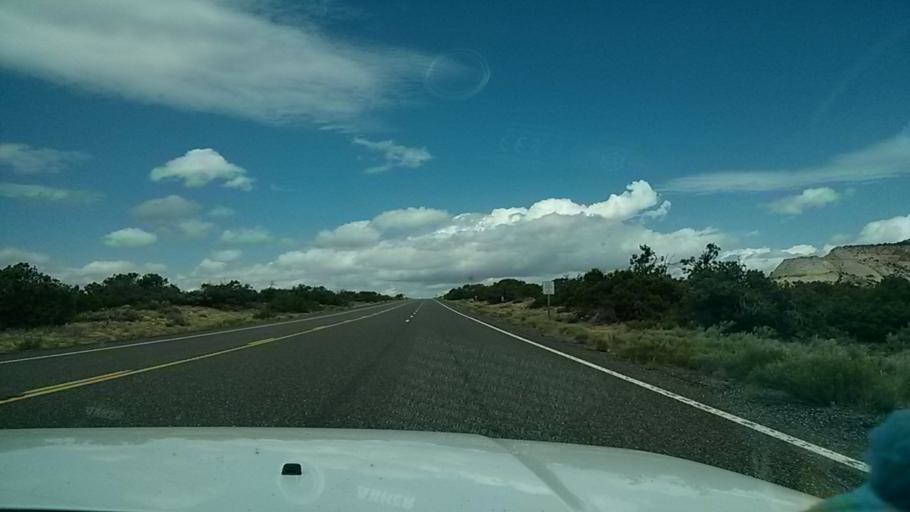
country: US
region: Utah
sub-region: Kane County
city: Kanab
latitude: 37.1700
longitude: -112.6110
